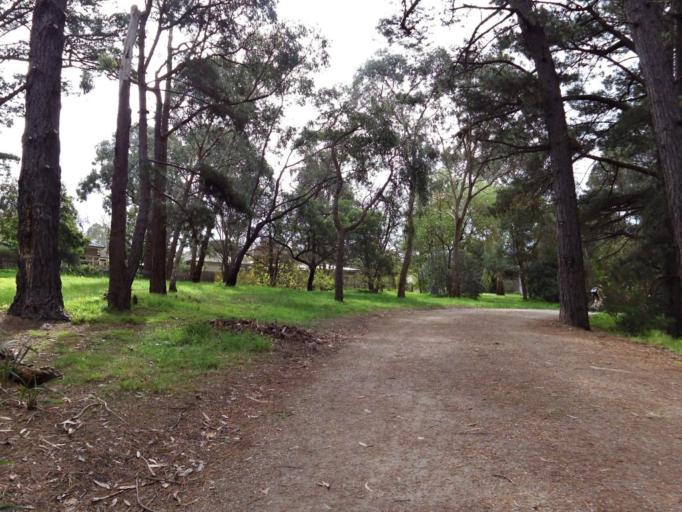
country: AU
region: Victoria
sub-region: Maroondah
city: Ringwood East
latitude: -37.7994
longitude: 145.2479
